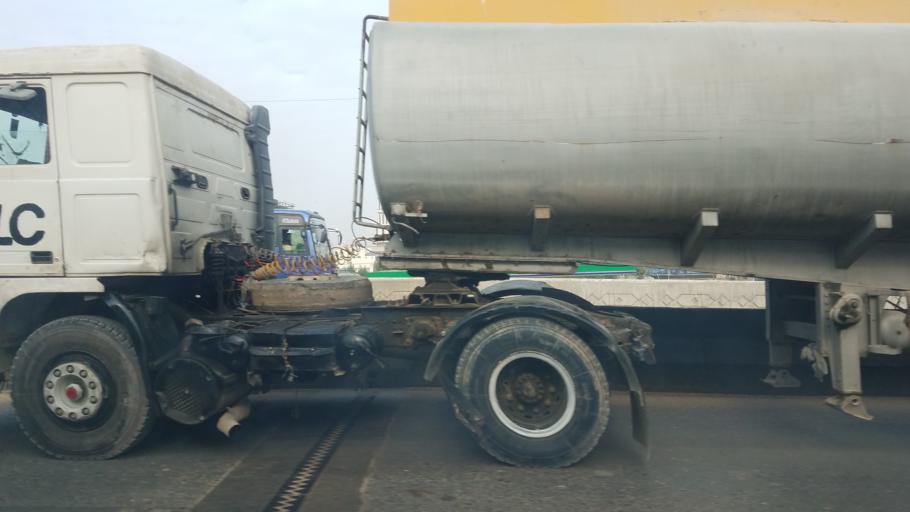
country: PK
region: Sindh
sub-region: Karachi District
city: Karachi
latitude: 24.9374
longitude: 67.0769
